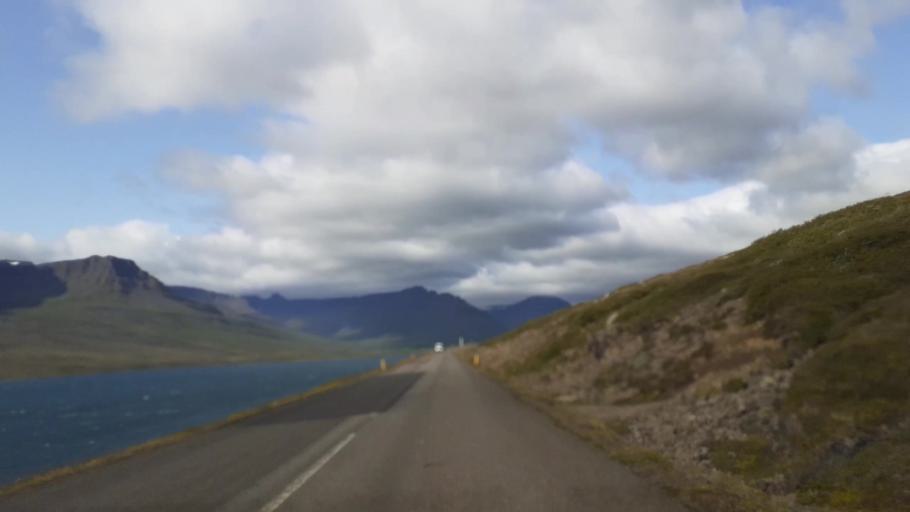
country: IS
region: East
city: Eskifjoerdur
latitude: 64.9219
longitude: -13.9676
